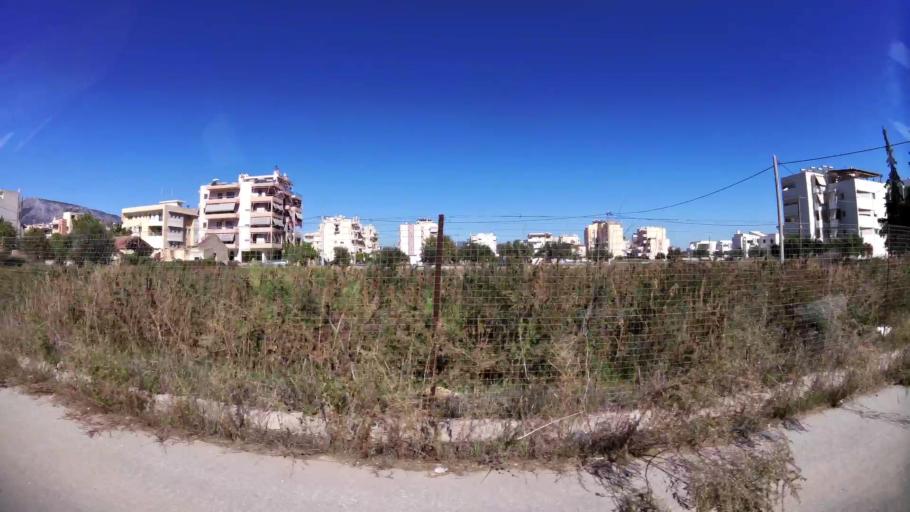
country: GR
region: Attica
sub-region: Nomarchia Anatolikis Attikis
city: Koropi
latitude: 37.9090
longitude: 23.8775
